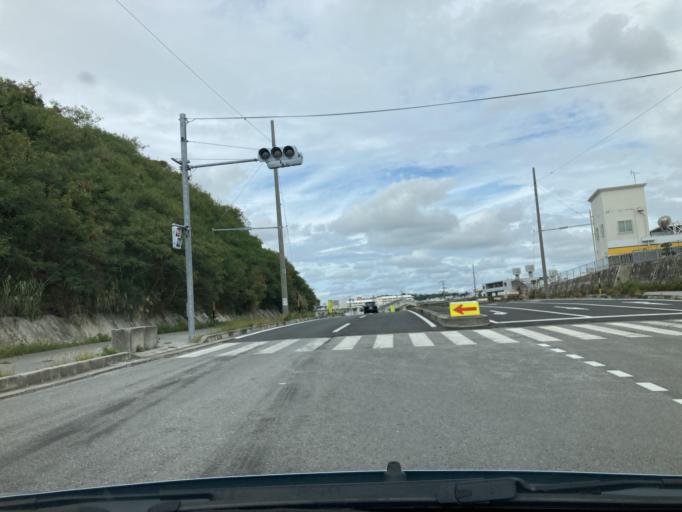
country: JP
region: Okinawa
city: Tomigusuku
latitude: 26.1687
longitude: 127.6773
